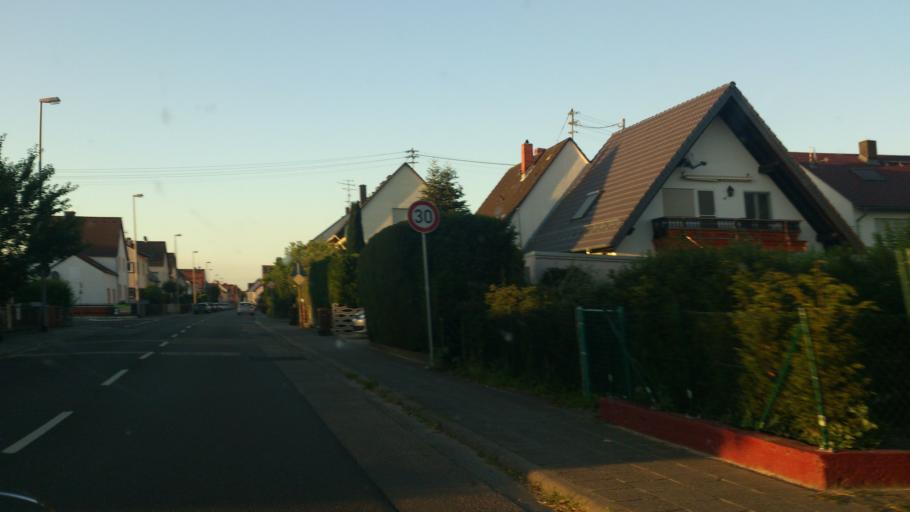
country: DE
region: Hesse
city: Raunheim
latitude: 50.0364
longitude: 8.4665
